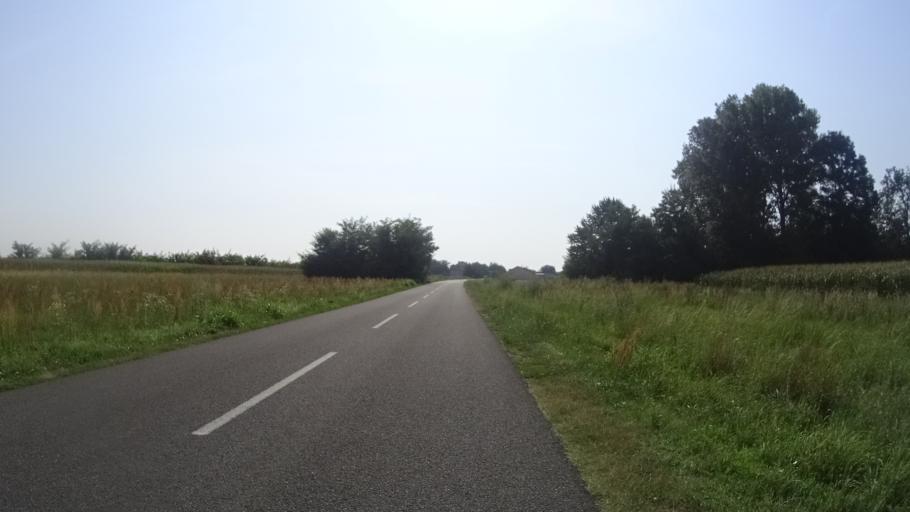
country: HR
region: Medimurska
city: Palovec
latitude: 46.3921
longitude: 16.5334
